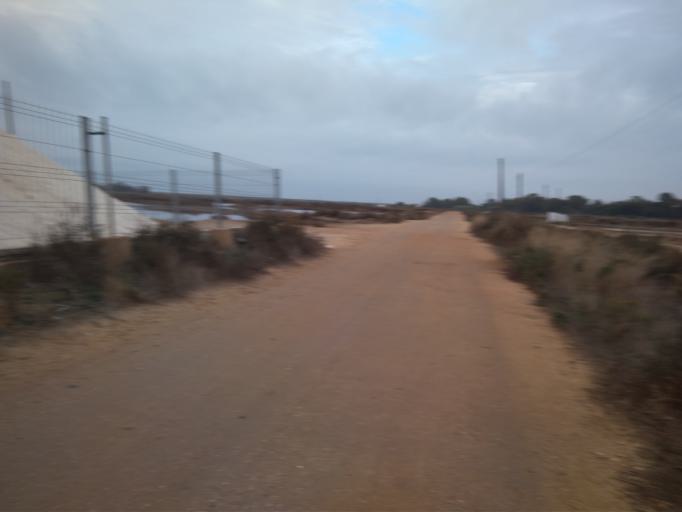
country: PT
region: Faro
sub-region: Loule
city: Almancil
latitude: 37.0305
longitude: -7.9988
